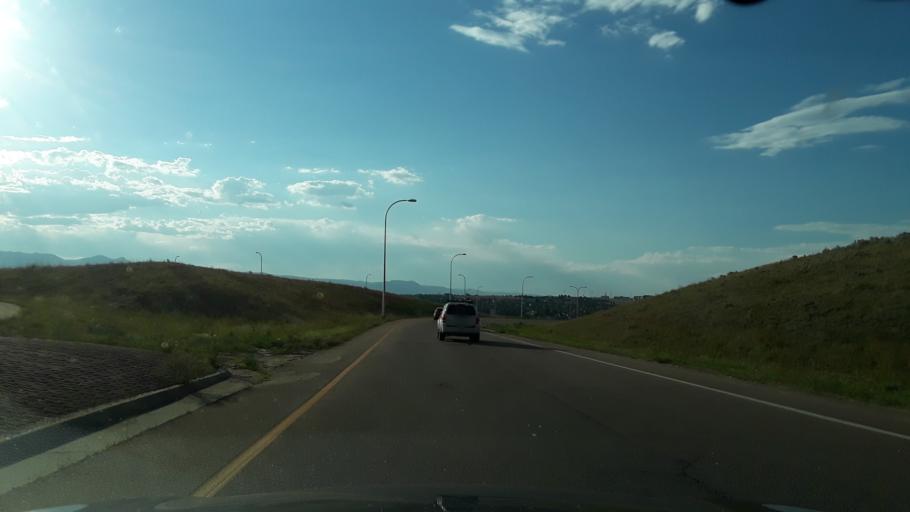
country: US
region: Colorado
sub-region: El Paso County
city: Black Forest
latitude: 38.9422
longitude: -104.7181
